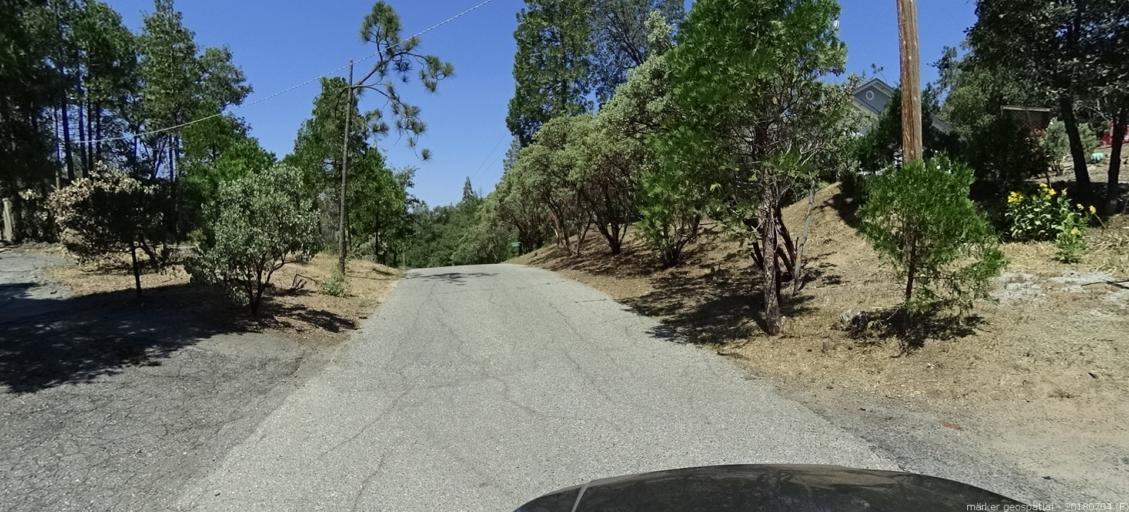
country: US
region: California
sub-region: Fresno County
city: Auberry
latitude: 37.2321
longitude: -119.4634
